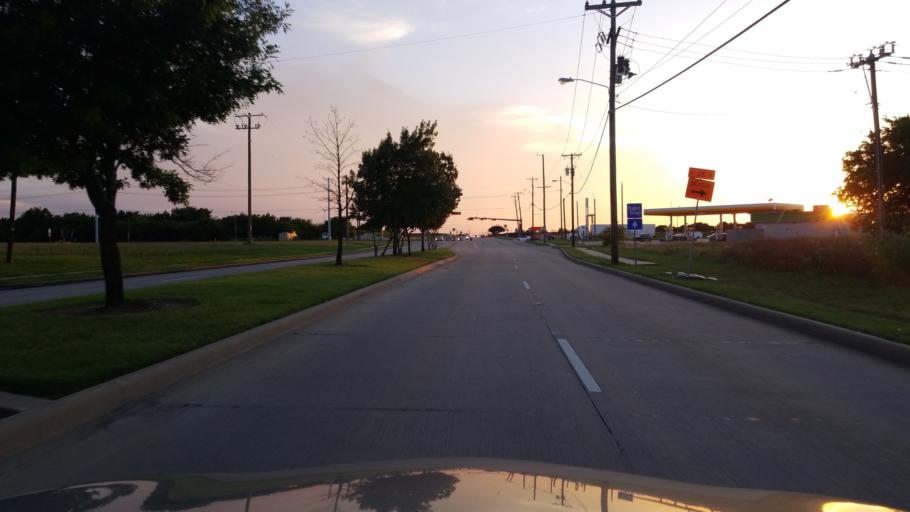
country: US
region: Texas
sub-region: Dallas County
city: Grand Prairie
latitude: 32.6914
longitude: -97.0422
